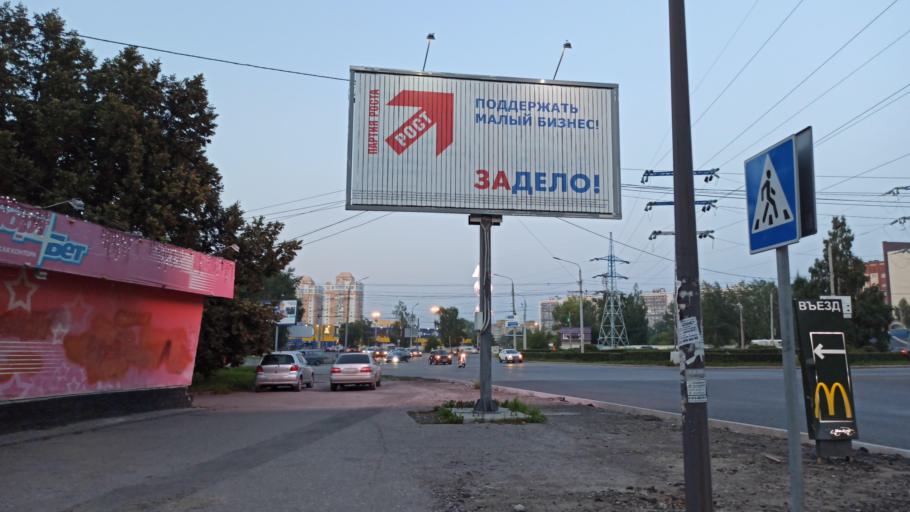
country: RU
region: Tomsk
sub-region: Tomskiy Rayon
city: Tomsk
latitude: 56.4554
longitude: 84.9740
